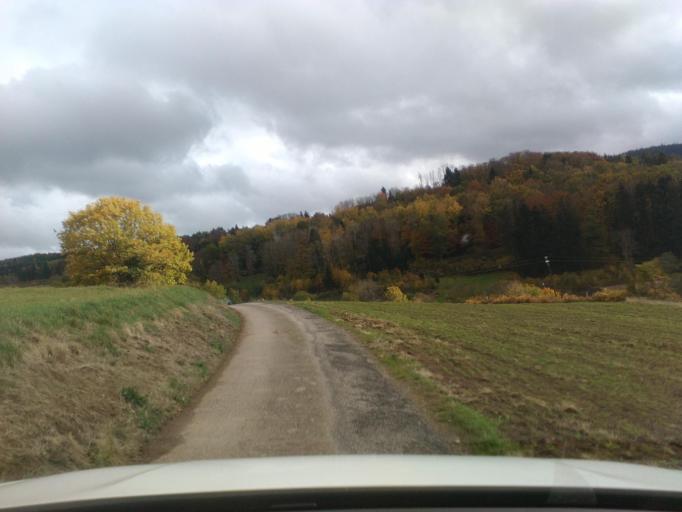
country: FR
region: Lorraine
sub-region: Departement des Vosges
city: Senones
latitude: 48.3362
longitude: 7.0198
